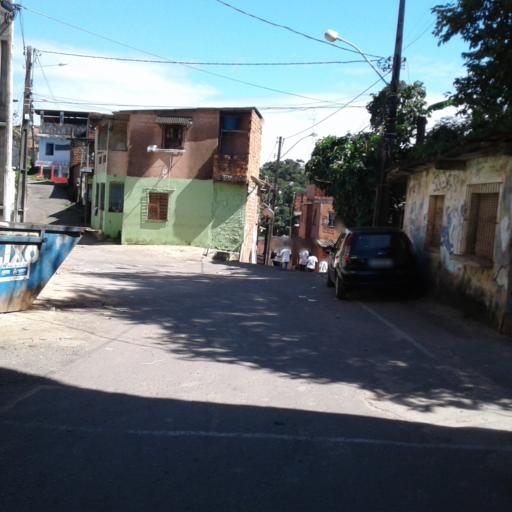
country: BR
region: Bahia
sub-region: Salvador
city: Salvador
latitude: -12.9113
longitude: -38.4669
